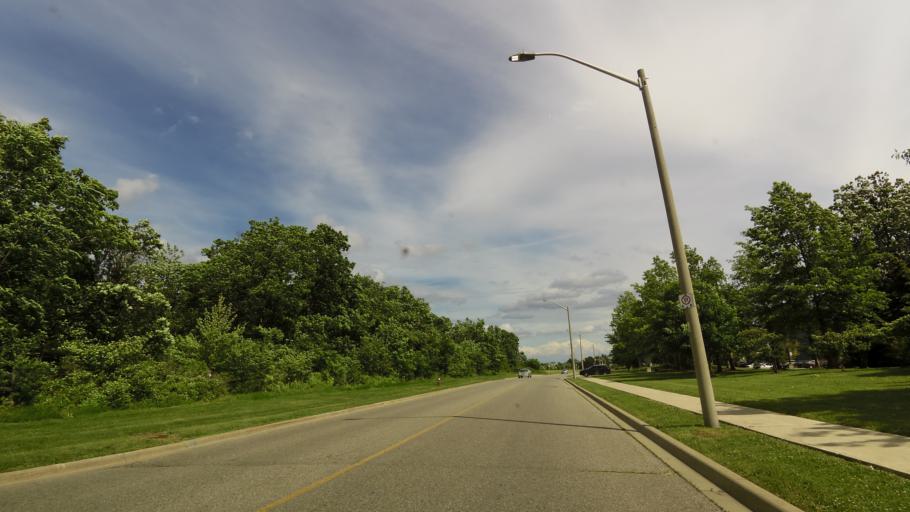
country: CA
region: Ontario
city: Mississauga
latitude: 43.5168
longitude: -79.6708
